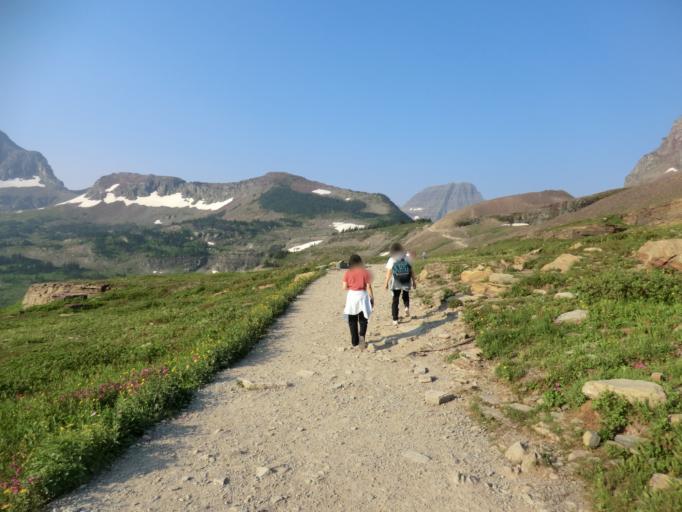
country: US
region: Montana
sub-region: Flathead County
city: Columbia Falls
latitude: 48.6923
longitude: -113.7291
